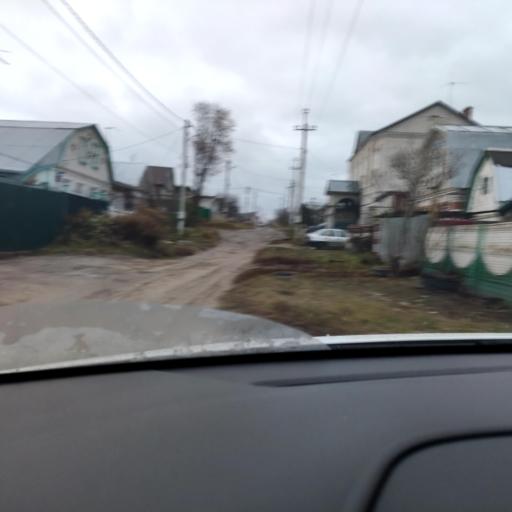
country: RU
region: Tatarstan
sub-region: Gorod Kazan'
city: Kazan
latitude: 55.8805
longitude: 49.0754
